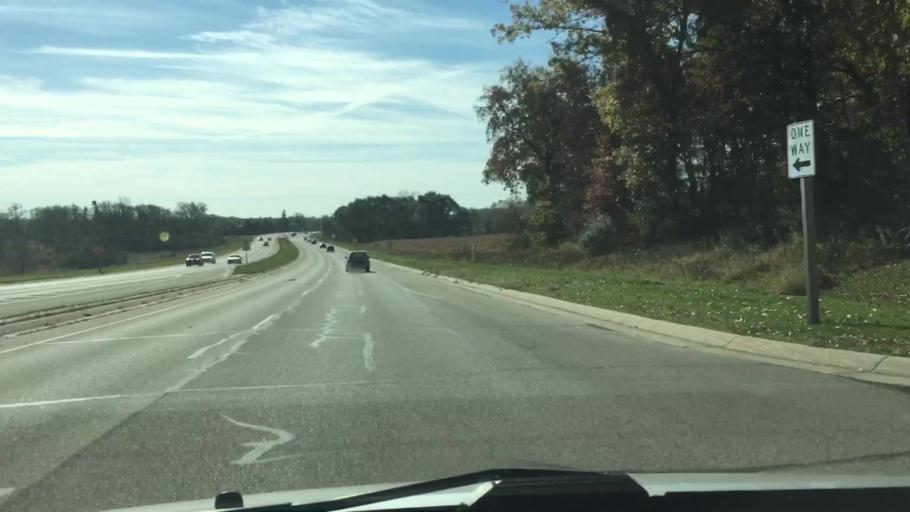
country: US
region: Wisconsin
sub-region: Waukesha County
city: Pewaukee
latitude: 43.1059
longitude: -88.2449
